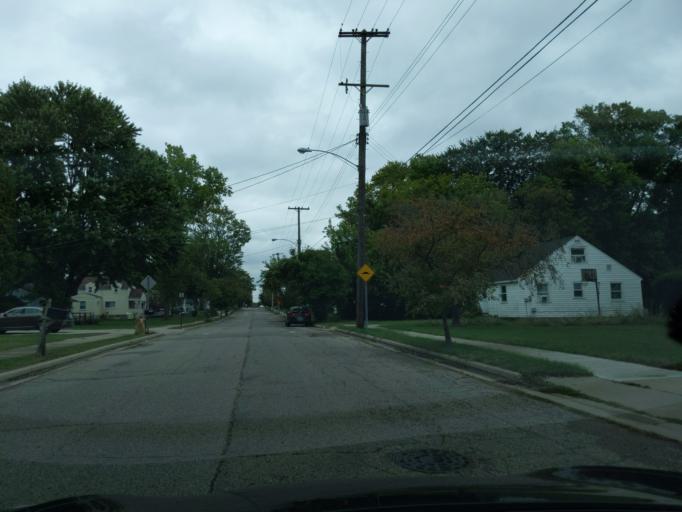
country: US
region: Michigan
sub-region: Ingham County
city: Lansing
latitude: 42.6879
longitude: -84.5711
